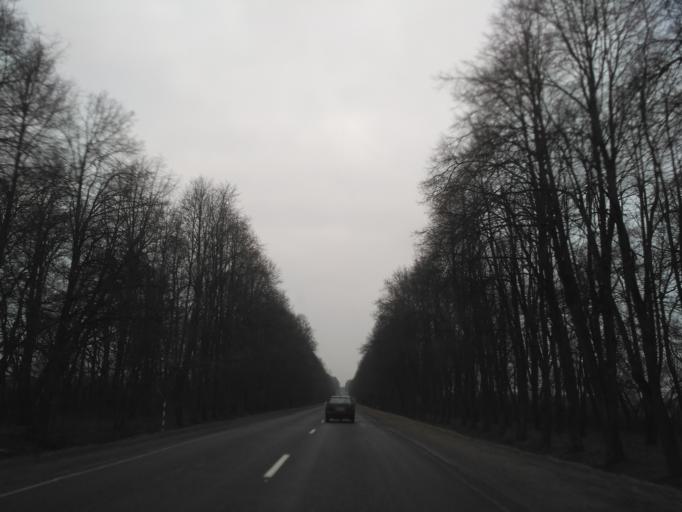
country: BY
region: Minsk
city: Snow
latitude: 53.2472
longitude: 26.2671
